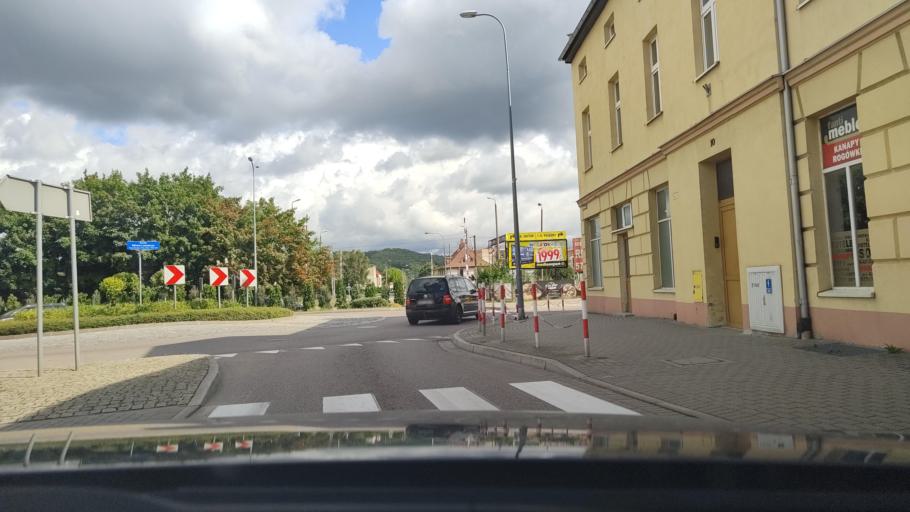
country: PL
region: Pomeranian Voivodeship
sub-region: Powiat wejherowski
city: Wejherowo
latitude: 54.6044
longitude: 18.2349
